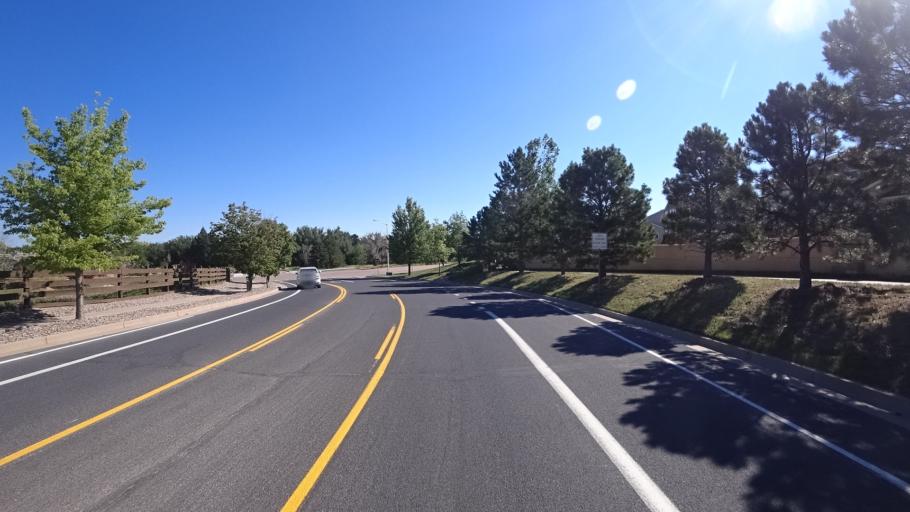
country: US
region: Colorado
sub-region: El Paso County
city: Black Forest
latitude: 38.9815
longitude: -104.7748
